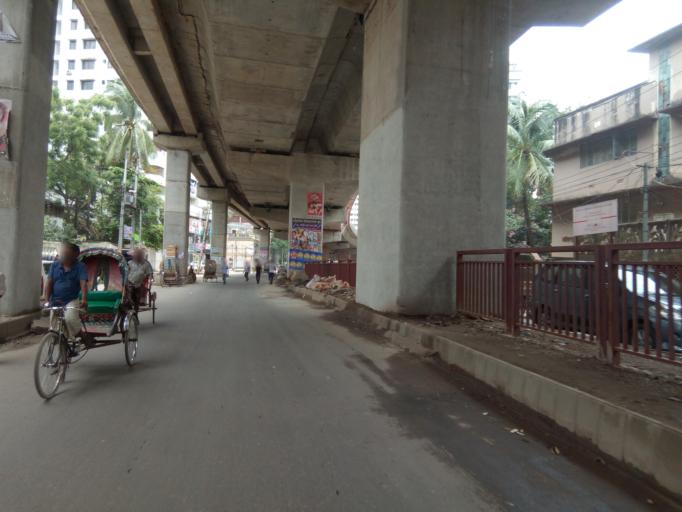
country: BD
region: Dhaka
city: Paltan
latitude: 23.7490
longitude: 90.4045
